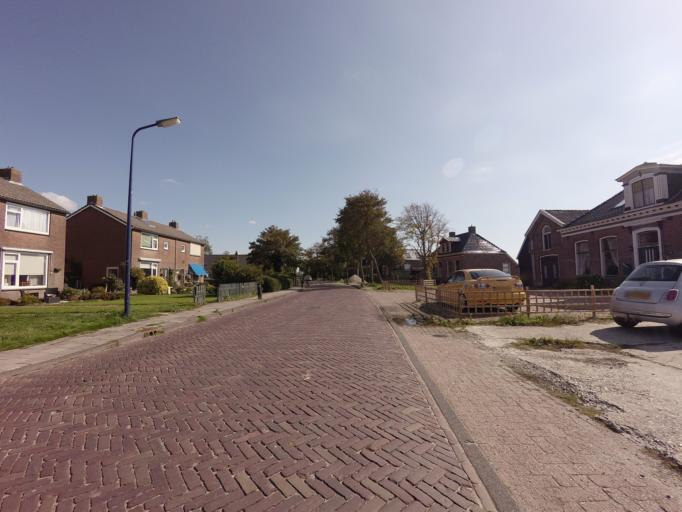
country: NL
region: Friesland
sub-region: Gemeente Littenseradiel
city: Makkum
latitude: 53.0999
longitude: 5.6462
